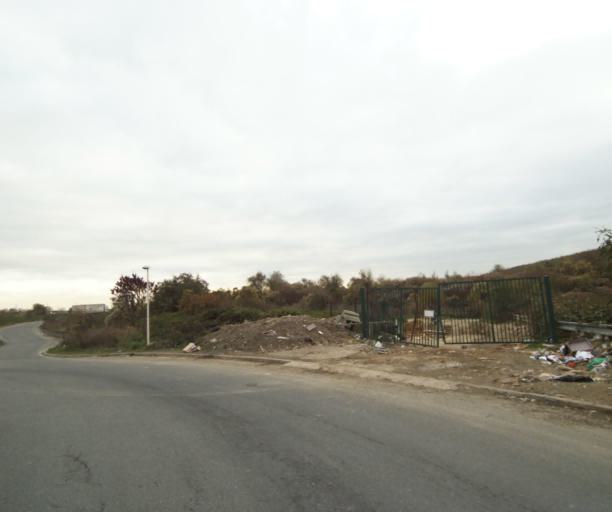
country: FR
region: Ile-de-France
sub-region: Departement du Val-d'Oise
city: Le Thillay
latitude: 48.9940
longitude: 2.4763
